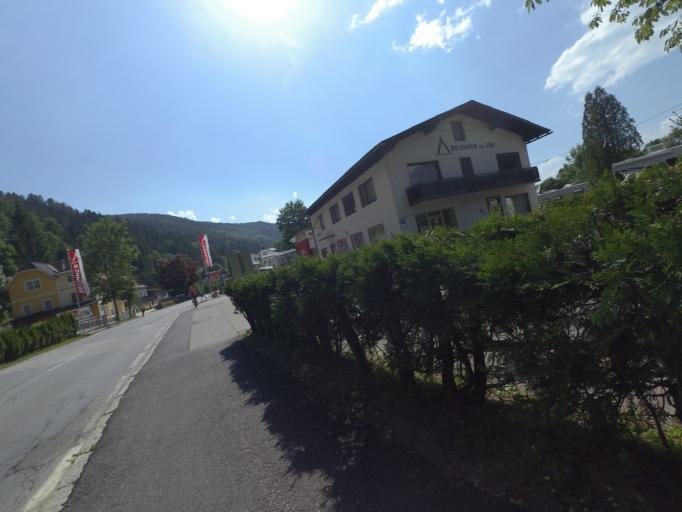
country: AT
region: Carinthia
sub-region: Politischer Bezirk Villach Land
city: Ferndorf
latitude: 46.7681
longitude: 13.6489
